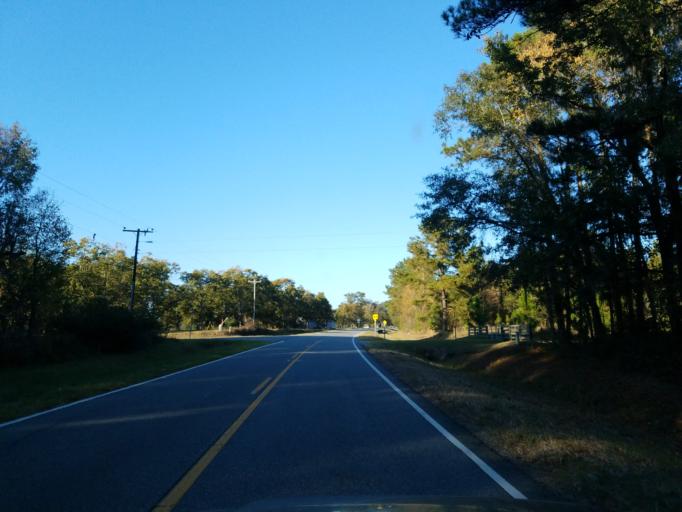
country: US
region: Georgia
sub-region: Lanier County
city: Lakeland
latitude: 30.9697
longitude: -83.0821
